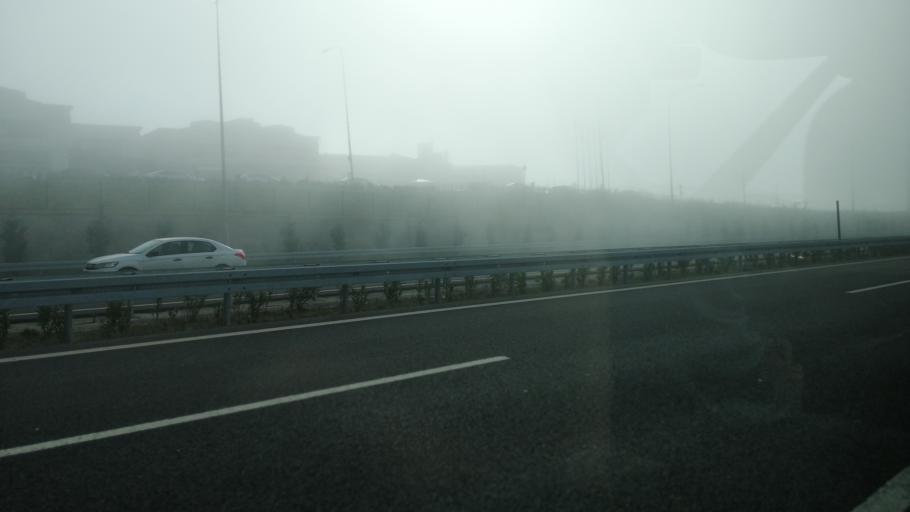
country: TR
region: Kocaeli
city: Tavsanli
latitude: 40.7729
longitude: 29.5184
